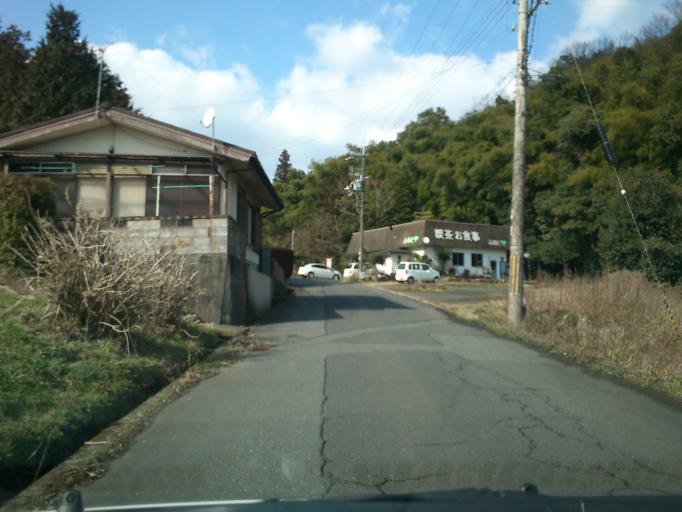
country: JP
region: Kyoto
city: Miyazu
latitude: 35.5797
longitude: 135.1781
